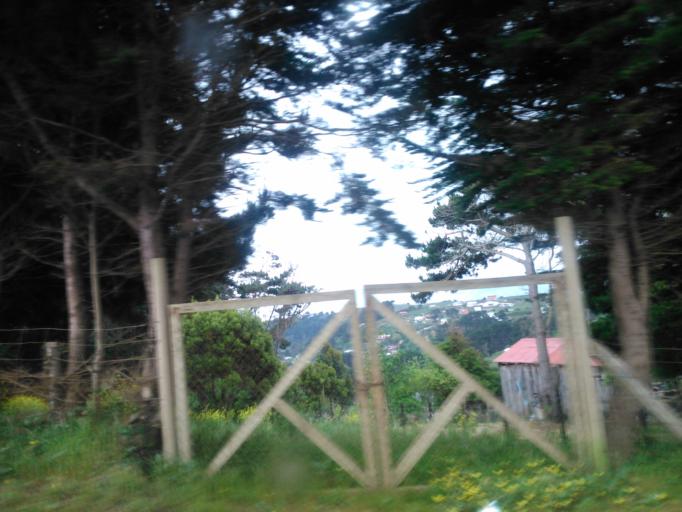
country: CL
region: Araucania
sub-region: Provincia de Cautin
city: Carahue
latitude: -38.8156
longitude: -73.4005
